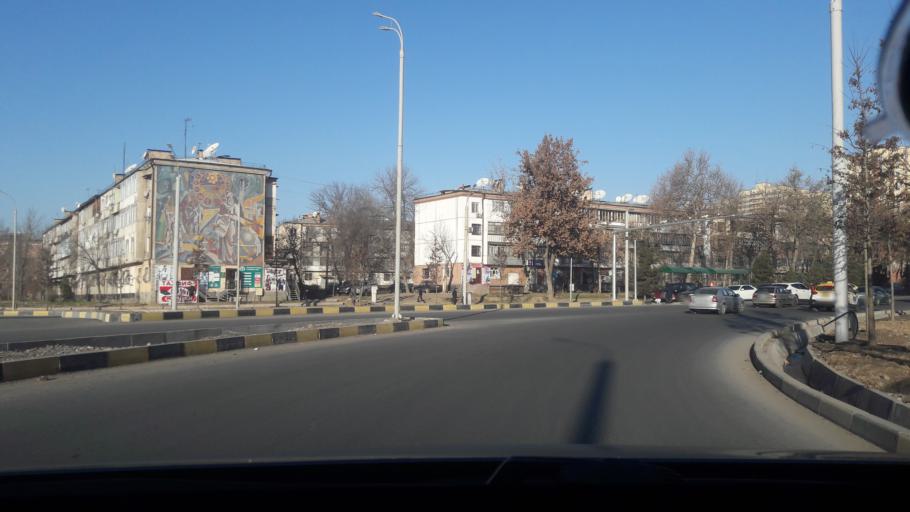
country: TJ
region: Dushanbe
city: Dushanbe
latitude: 38.5587
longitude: 68.7554
